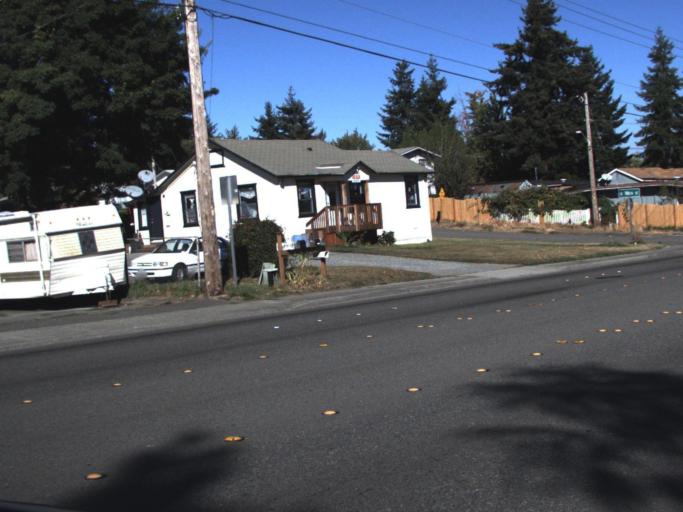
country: US
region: Washington
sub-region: King County
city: East Hill-Meridian
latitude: 47.4360
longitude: -122.1970
